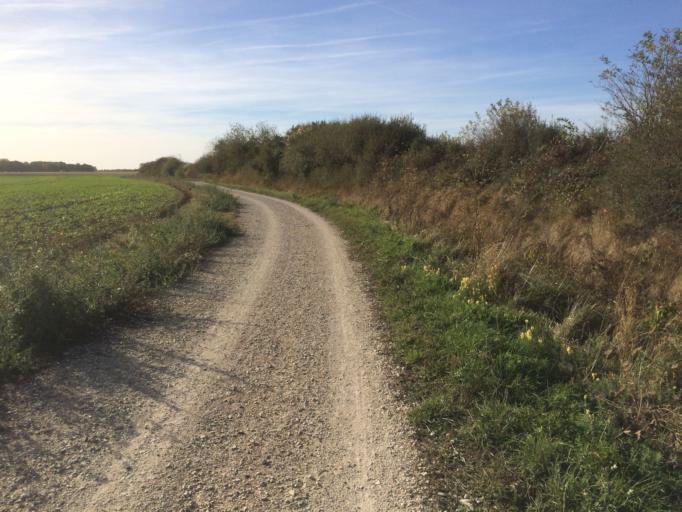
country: FR
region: Ile-de-France
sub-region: Departement de l'Essonne
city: Vauhallan
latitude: 48.7223
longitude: 2.2171
